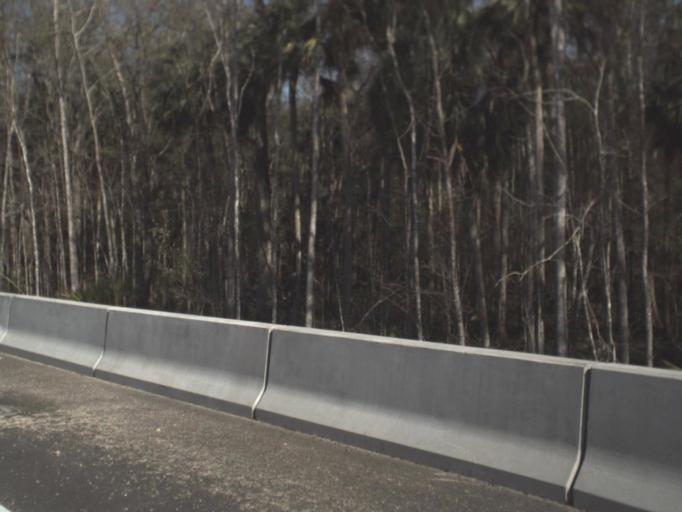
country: US
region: Florida
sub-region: Leon County
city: Woodville
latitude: 30.1471
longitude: -83.9750
